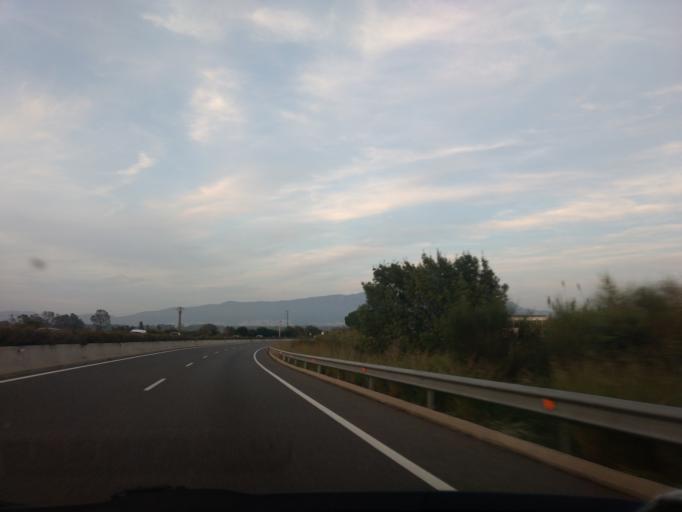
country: ES
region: Catalonia
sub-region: Provincia de Girona
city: Castello d'Empuries
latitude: 42.2575
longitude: 3.0886
